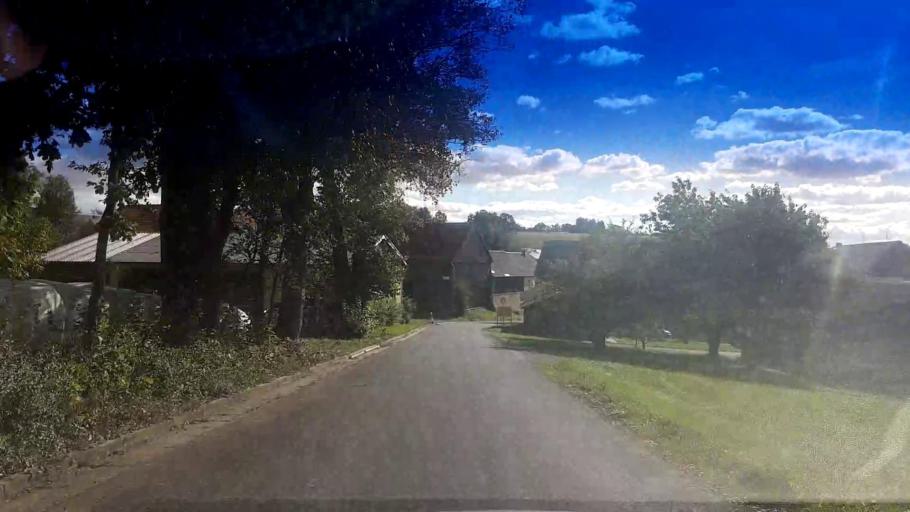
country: DE
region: Bavaria
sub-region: Upper Franconia
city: Arzberg
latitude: 50.0240
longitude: 12.2171
